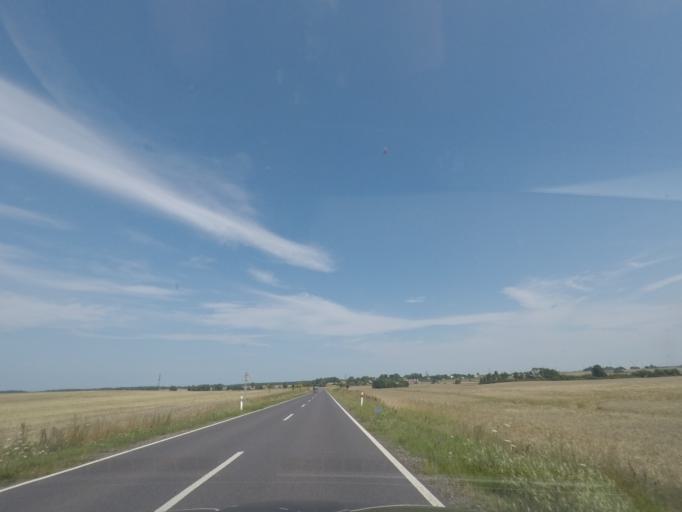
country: PL
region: West Pomeranian Voivodeship
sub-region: Powiat koszalinski
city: Sianow
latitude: 54.2840
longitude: 16.2711
